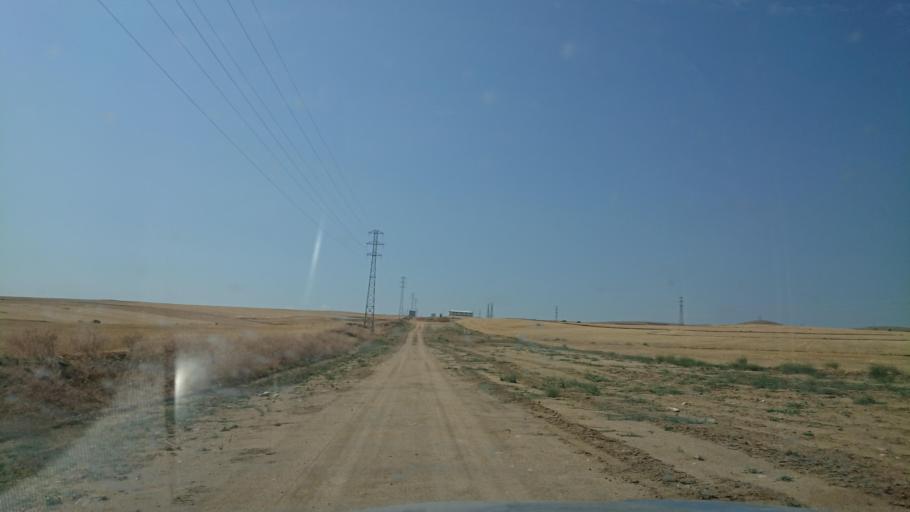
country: TR
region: Aksaray
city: Sariyahsi
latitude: 38.9548
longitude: 33.9130
